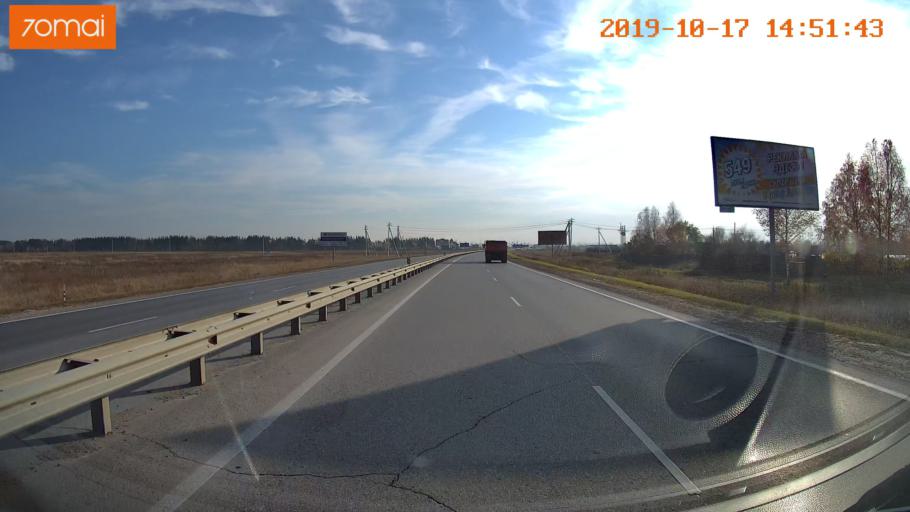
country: RU
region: Rjazan
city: Polyany
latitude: 54.7149
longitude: 39.8482
